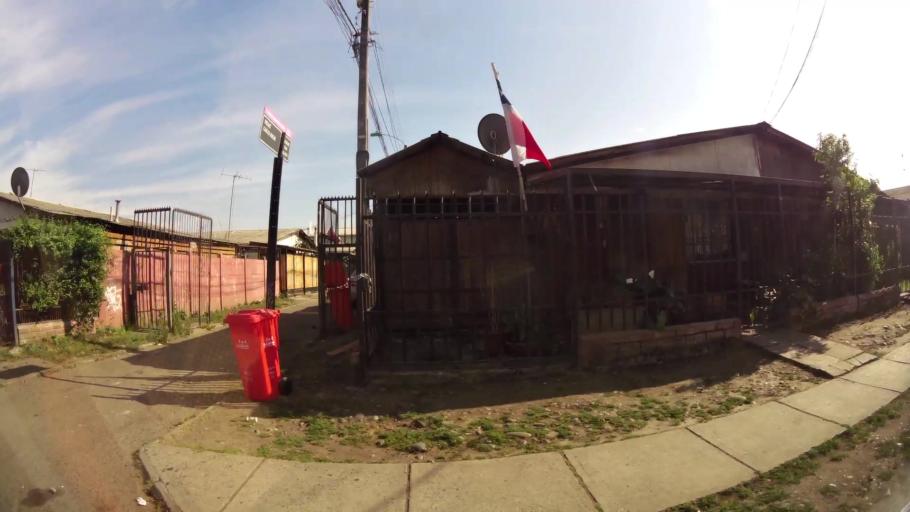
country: CL
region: Santiago Metropolitan
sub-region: Provincia de Talagante
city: Talagante
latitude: -33.6788
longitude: -70.9470
